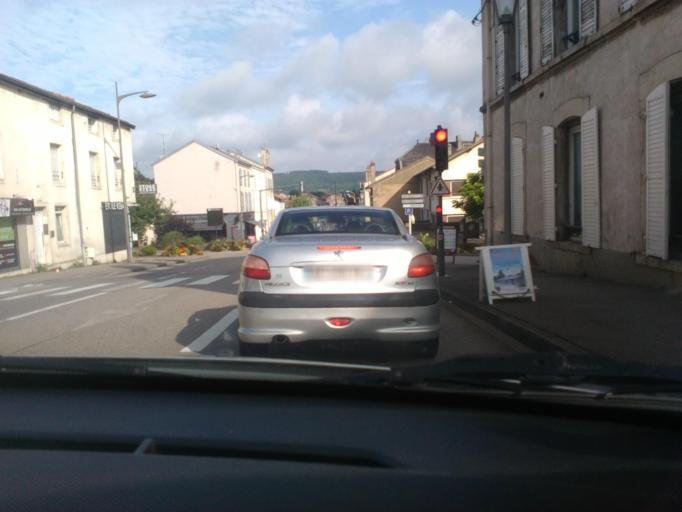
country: FR
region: Lorraine
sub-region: Departement de Meurthe-et-Moselle
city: Frouard
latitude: 48.7547
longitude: 6.1417
